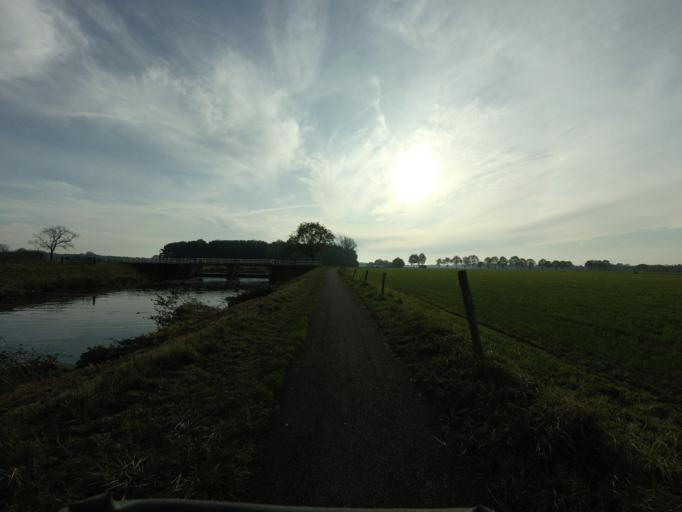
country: NL
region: North Brabant
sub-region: Gemeente Breda
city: Breda
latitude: 51.5224
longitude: 4.7852
